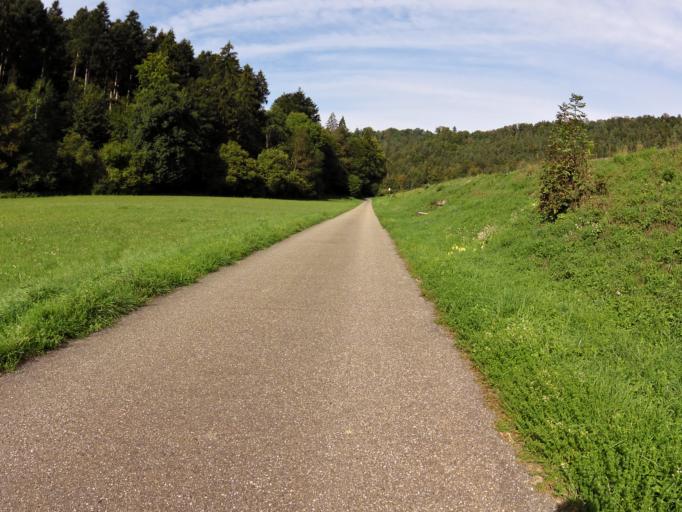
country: DE
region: Baden-Wuerttemberg
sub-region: Karlsruhe Region
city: Horb am Neckar
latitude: 48.4523
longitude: 8.7524
